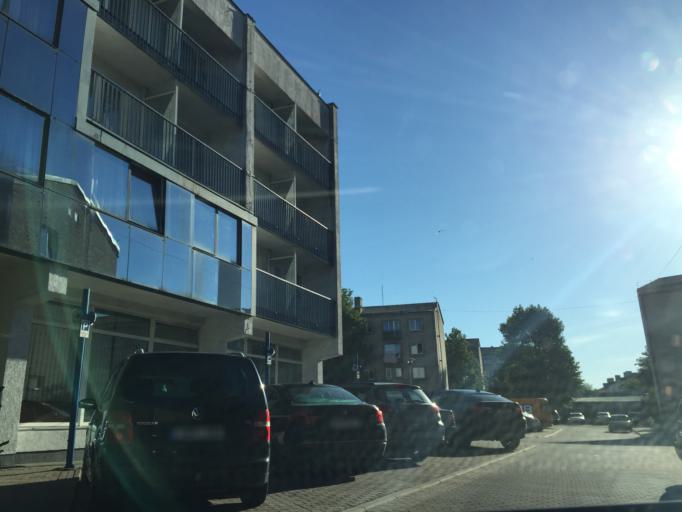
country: LV
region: Ventspils
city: Ventspils
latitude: 57.4030
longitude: 21.5819
